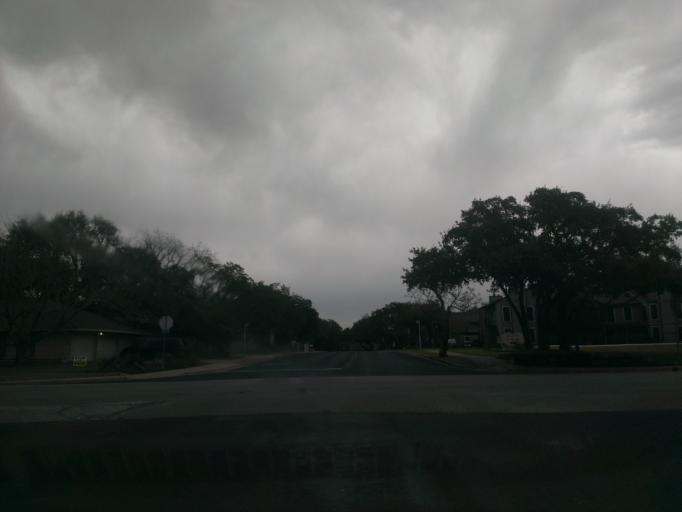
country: US
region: Texas
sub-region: Travis County
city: West Lake Hills
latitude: 30.3590
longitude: -97.7541
